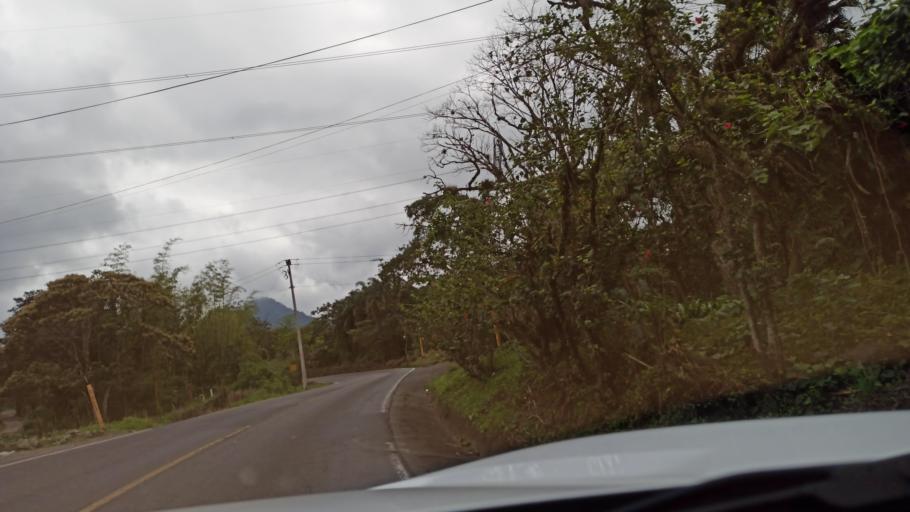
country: MX
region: Veracruz
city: Cuautlapan
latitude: 18.8895
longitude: -97.0107
